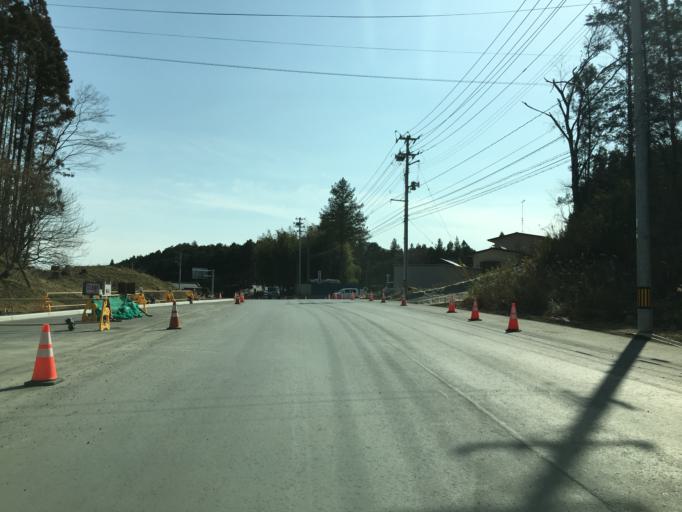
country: JP
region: Ibaraki
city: Daigo
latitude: 36.8472
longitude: 140.4334
